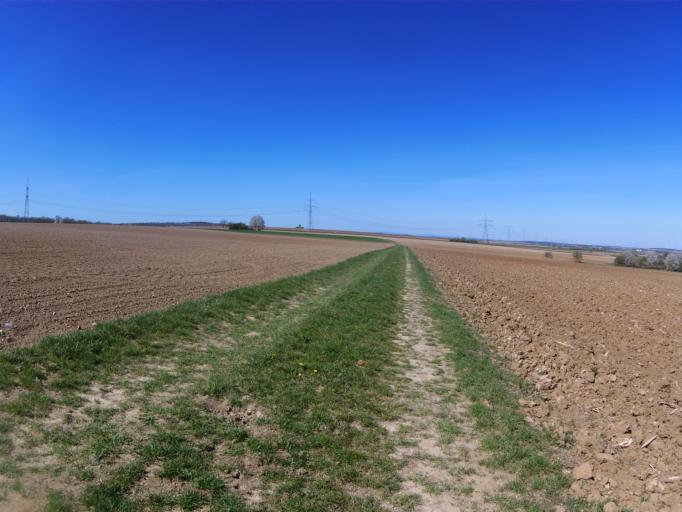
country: DE
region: Bavaria
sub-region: Regierungsbezirk Unterfranken
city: Biebelried
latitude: 49.8053
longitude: 10.0826
